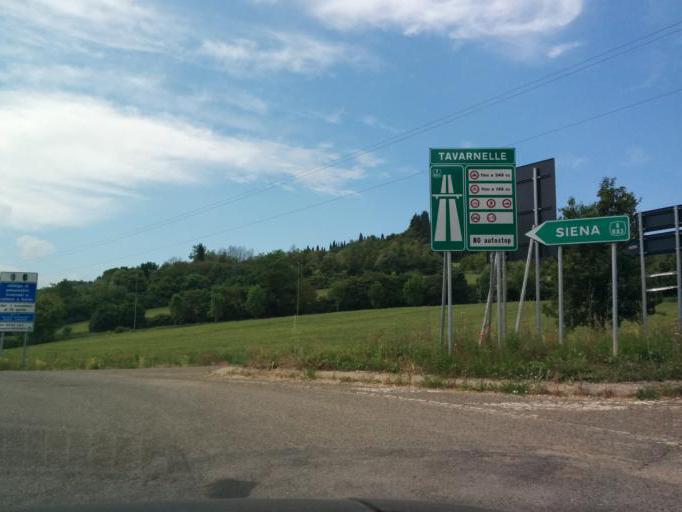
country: IT
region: Tuscany
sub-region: Province of Florence
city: Sambuca
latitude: 43.5929
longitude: 11.1976
